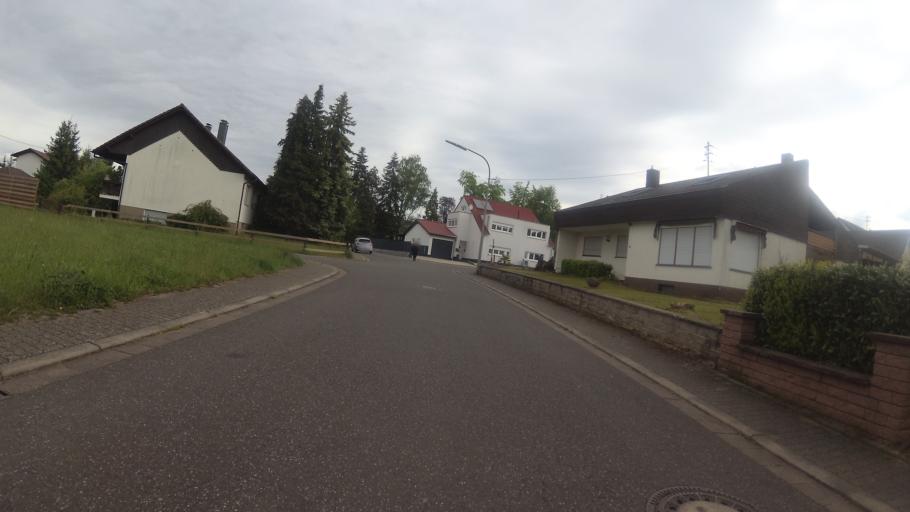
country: LU
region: Grevenmacher
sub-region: Canton de Remich
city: Remich
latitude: 49.5325
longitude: 6.3830
